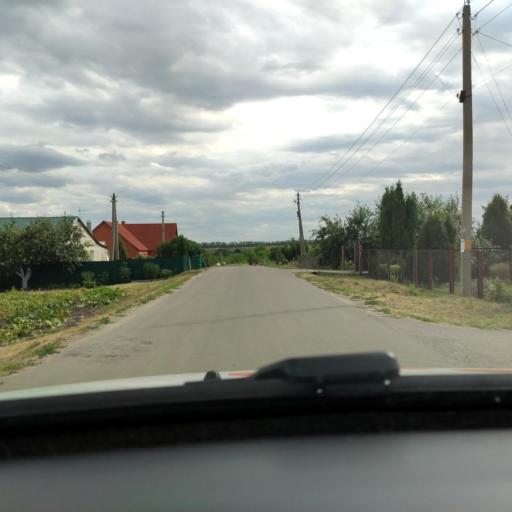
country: RU
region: Voronezj
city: Orlovo
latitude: 51.6527
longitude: 39.5715
